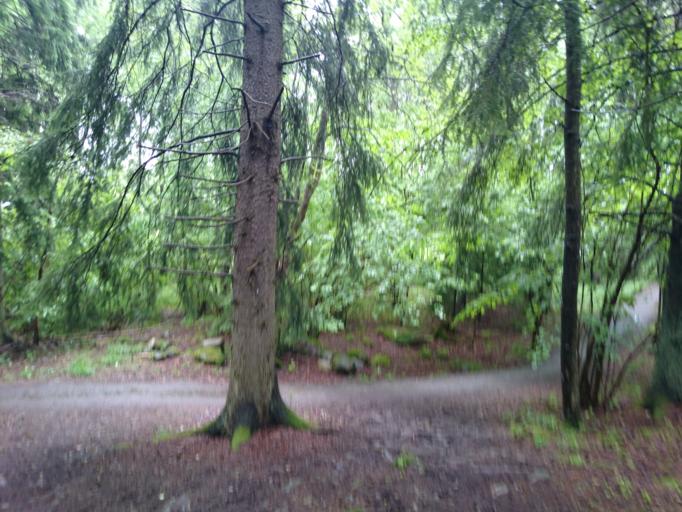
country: SE
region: Stockholm
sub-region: Huddinge Kommun
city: Segeltorp
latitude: 59.2705
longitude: 17.9316
